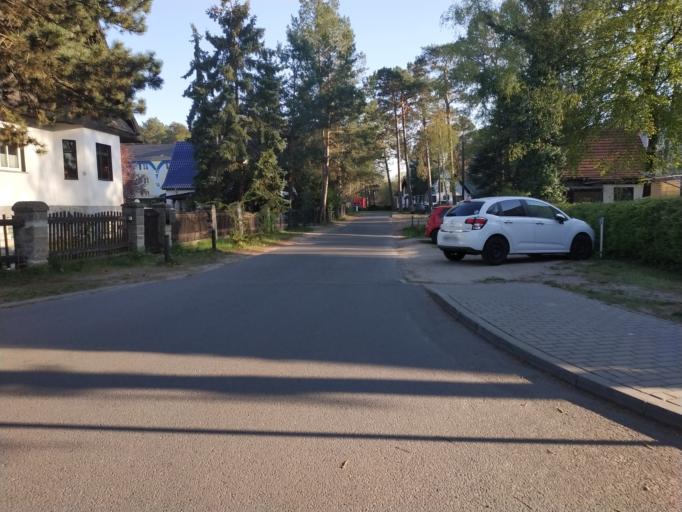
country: DE
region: Brandenburg
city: Petershagen
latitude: 52.5416
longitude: 13.8319
